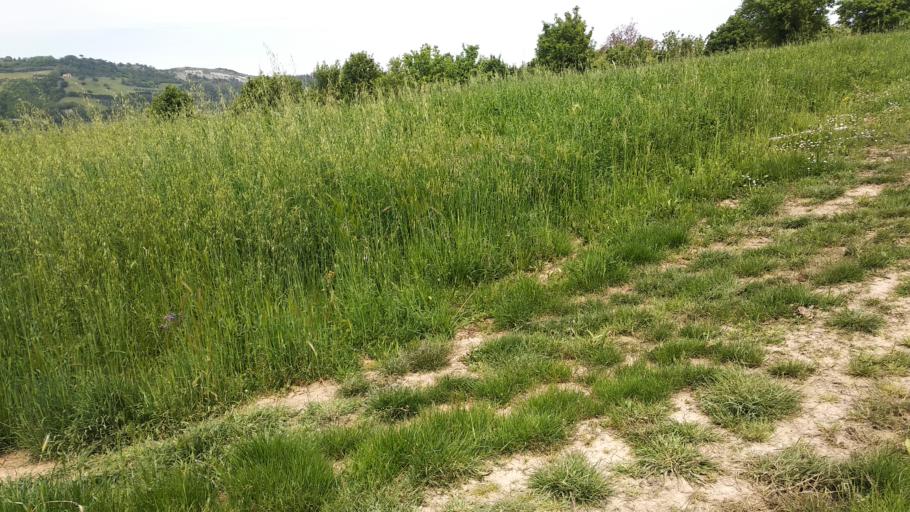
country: IT
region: Emilia-Romagna
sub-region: Provincia di Ravenna
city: Brisighella
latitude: 44.2045
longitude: 11.7632
